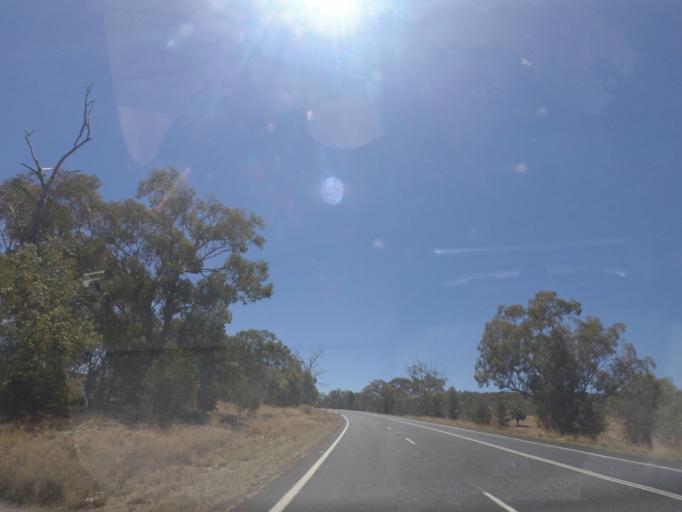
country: AU
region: New South Wales
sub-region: Warrumbungle Shire
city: Coonabarabran
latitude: -31.4657
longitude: 148.9634
